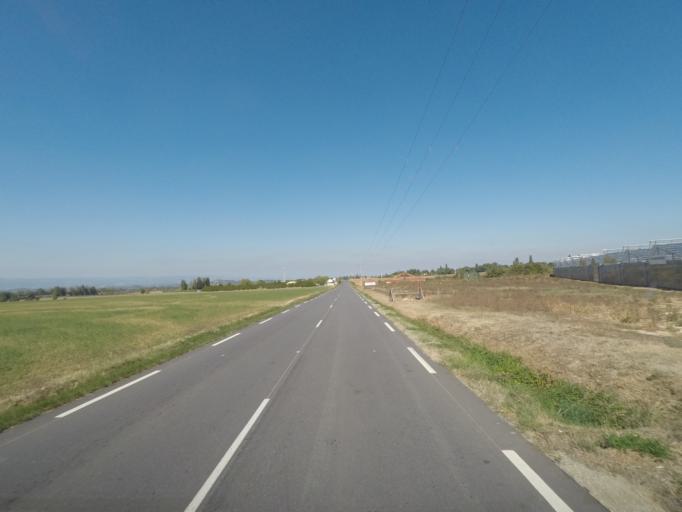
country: FR
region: Rhone-Alpes
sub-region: Departement de la Drome
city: Upie
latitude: 44.8002
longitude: 5.0166
